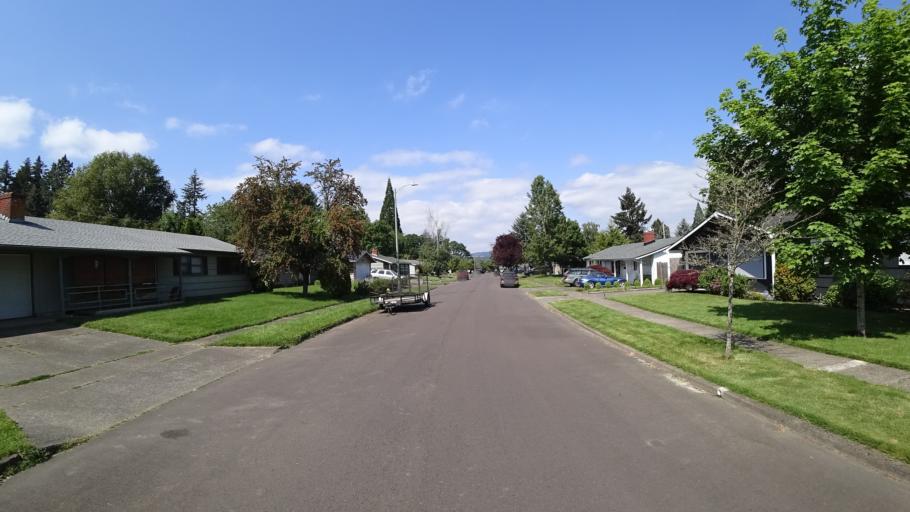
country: US
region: Oregon
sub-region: Washington County
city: Beaverton
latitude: 45.4711
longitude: -122.7935
